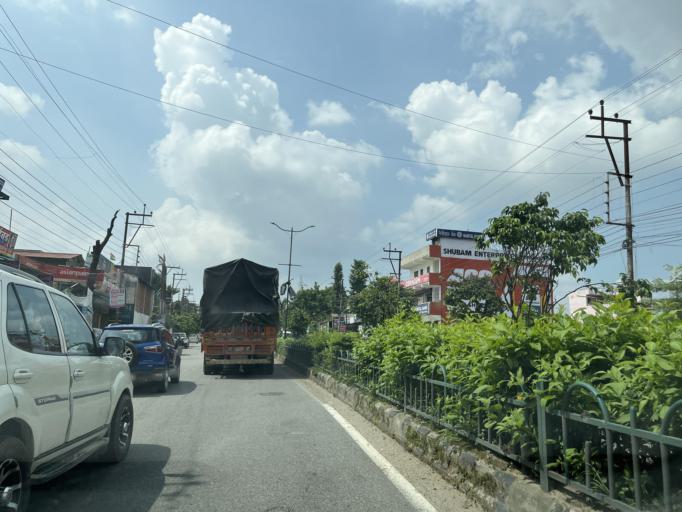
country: IN
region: Uttarakhand
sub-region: Dehradun
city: Raipur
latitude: 30.2812
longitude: 78.0714
